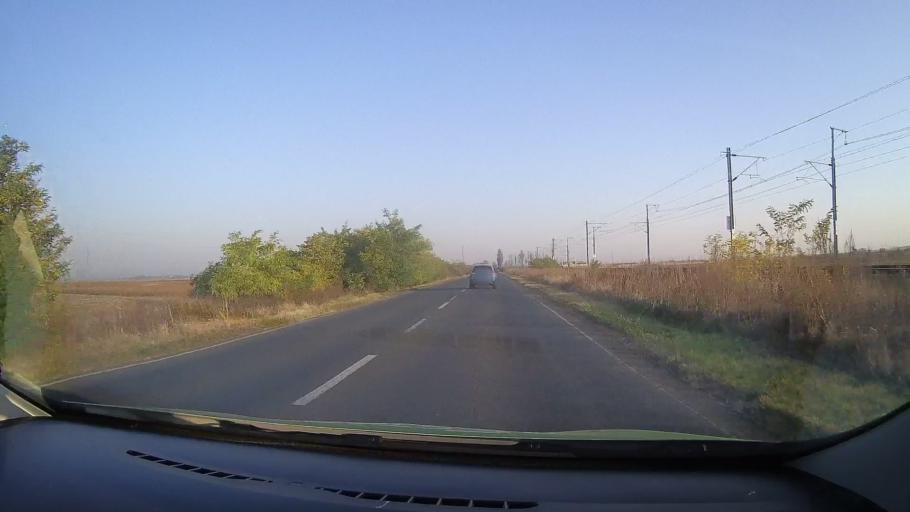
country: RO
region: Arad
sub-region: Comuna Sofronea
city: Sofronea
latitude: 46.2581
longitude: 21.3178
